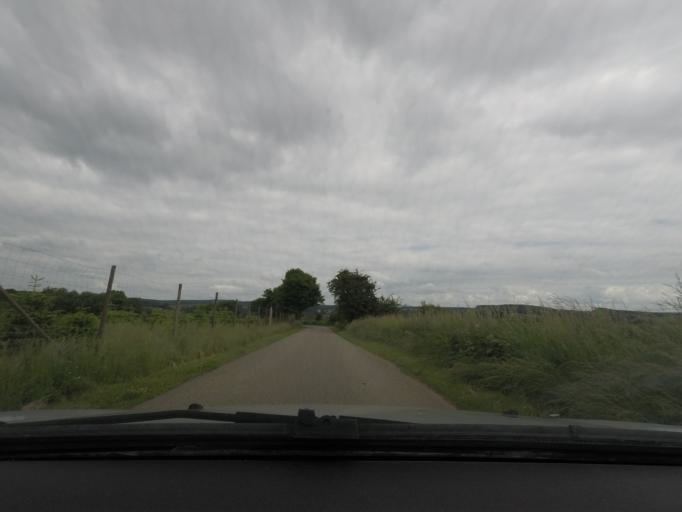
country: BE
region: Wallonia
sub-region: Province du Luxembourg
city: Leglise
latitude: 49.8152
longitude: 5.5271
